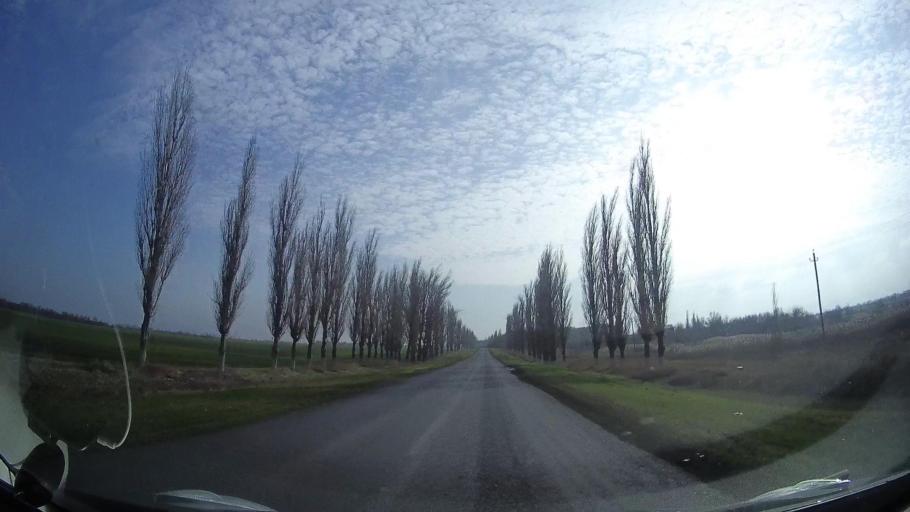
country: RU
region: Rostov
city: Mechetinskaya
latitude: 46.8307
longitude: 40.5512
